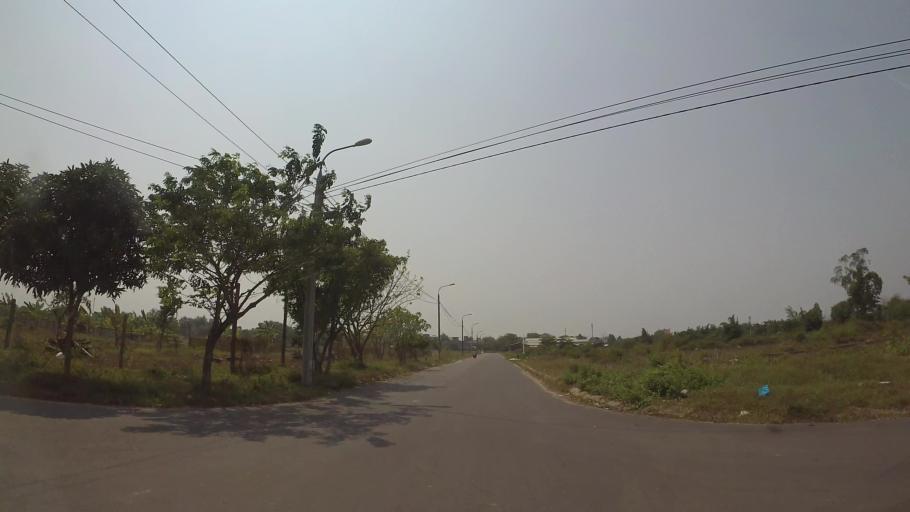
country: VN
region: Da Nang
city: Cam Le
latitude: 15.9794
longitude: 108.2115
